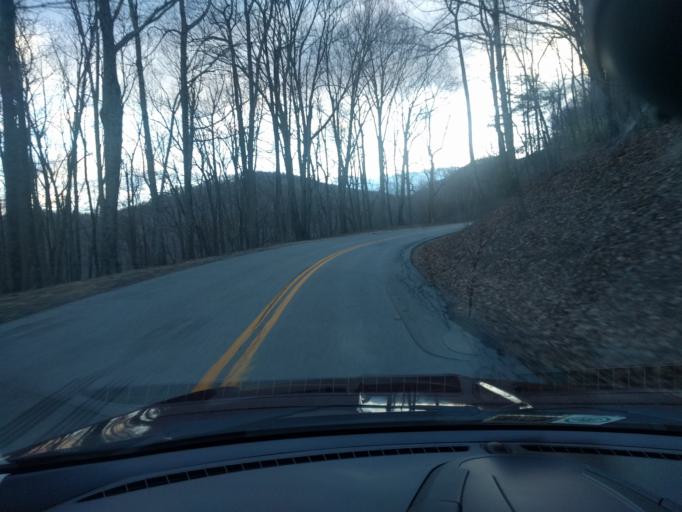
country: US
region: Virginia
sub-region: Botetourt County
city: Buchanan
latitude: 37.4718
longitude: -79.6406
